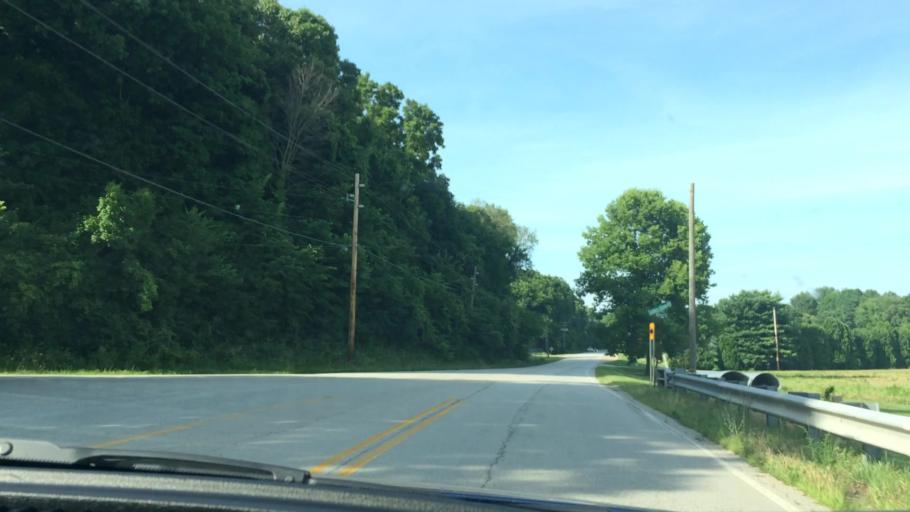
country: US
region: Indiana
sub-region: Tippecanoe County
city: Battle Ground
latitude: 40.4819
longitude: -86.8812
